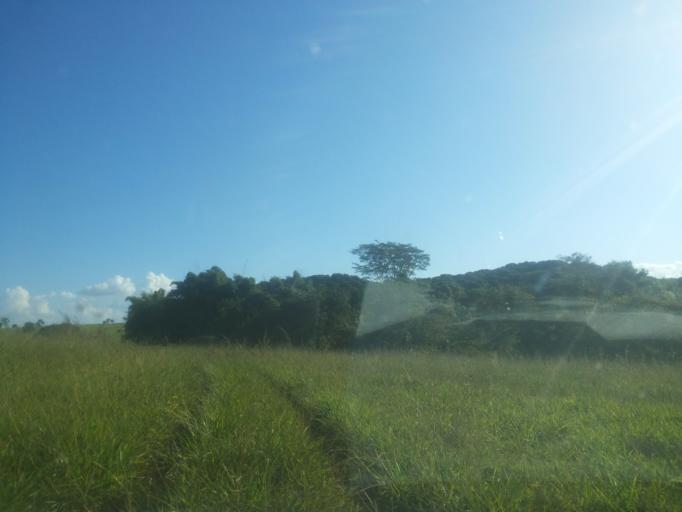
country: BR
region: Minas Gerais
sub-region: Santa Vitoria
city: Santa Vitoria
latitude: -19.0000
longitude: -50.4471
